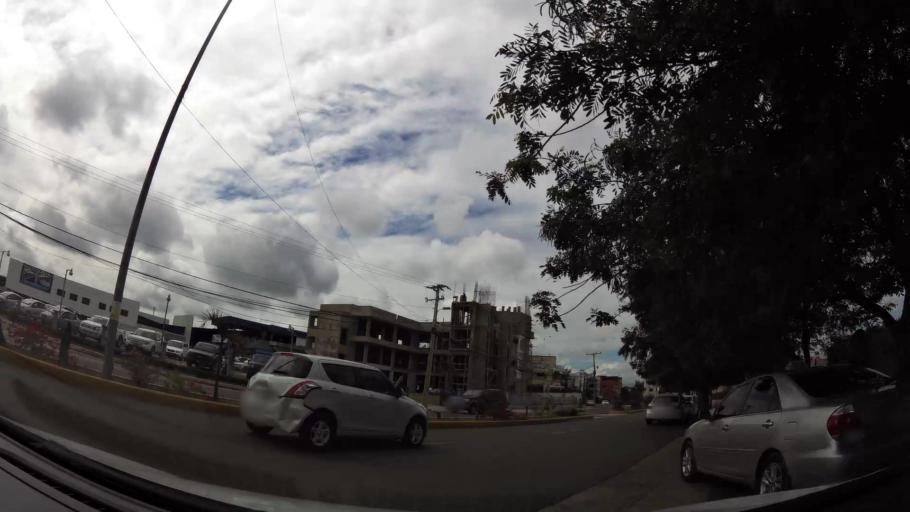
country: DO
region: Santiago
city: Santiago de los Caballeros
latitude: 19.4443
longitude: -70.6719
